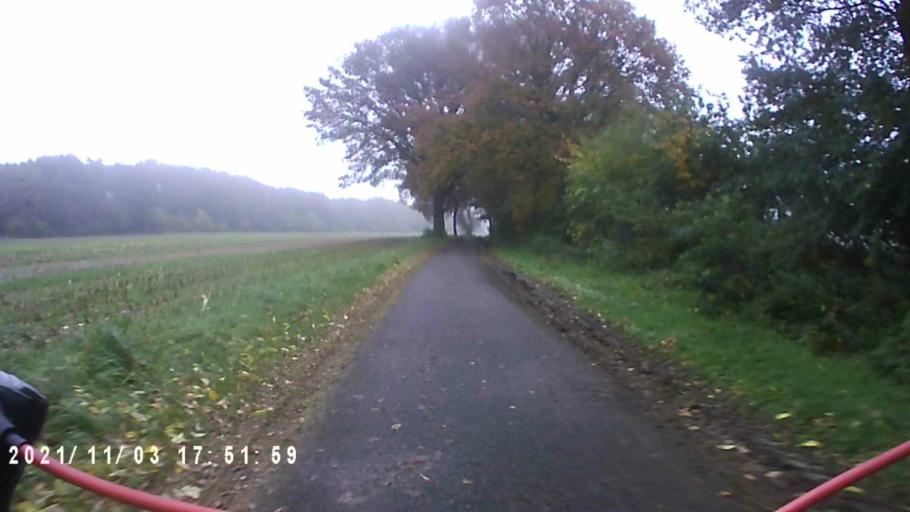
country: NL
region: Drenthe
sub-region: Gemeente Westerveld
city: Dwingeloo
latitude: 52.8399
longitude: 6.3132
